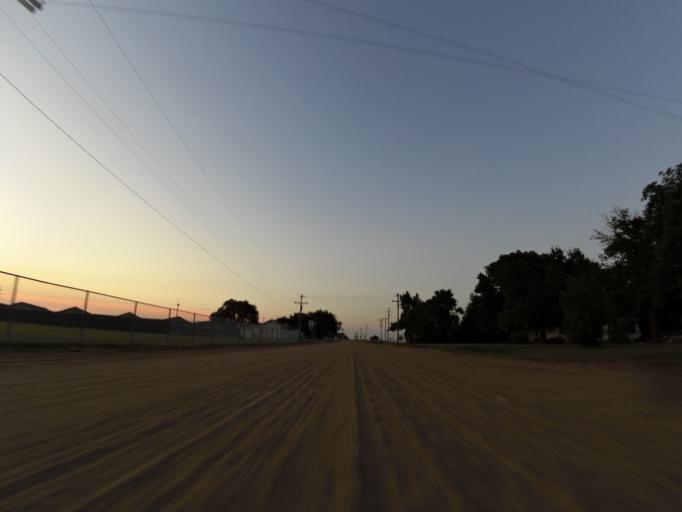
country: US
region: Kansas
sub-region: Reno County
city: South Hutchinson
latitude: 37.9951
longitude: -98.0320
